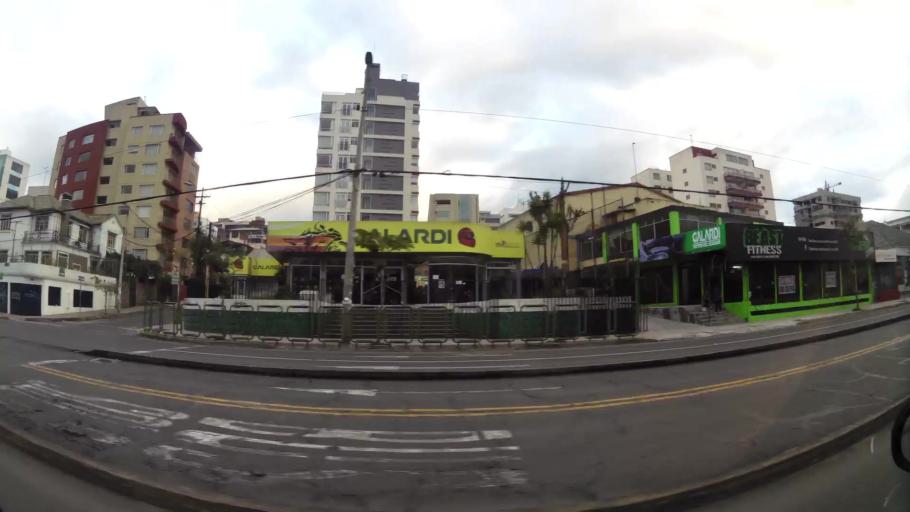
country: EC
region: Pichincha
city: Quito
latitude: -0.2034
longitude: -78.4882
